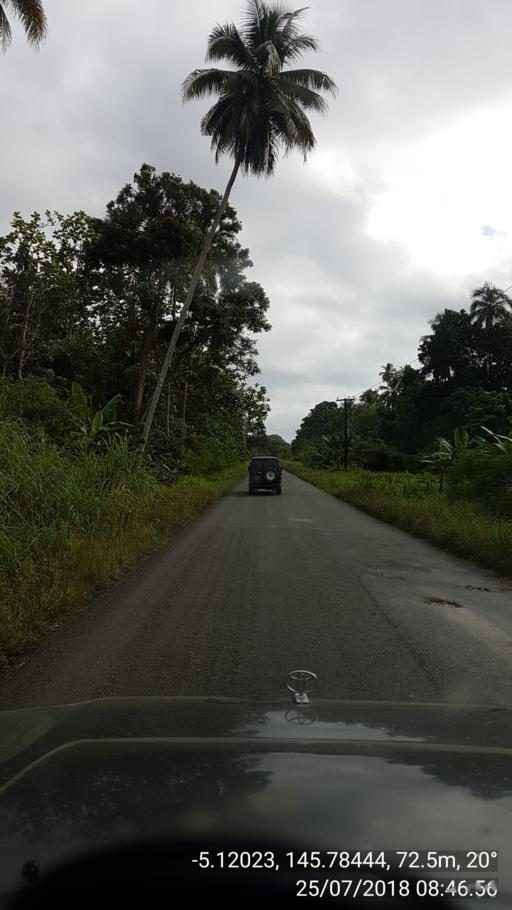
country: PG
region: Madang
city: Madang
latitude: -5.1203
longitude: 145.7844
